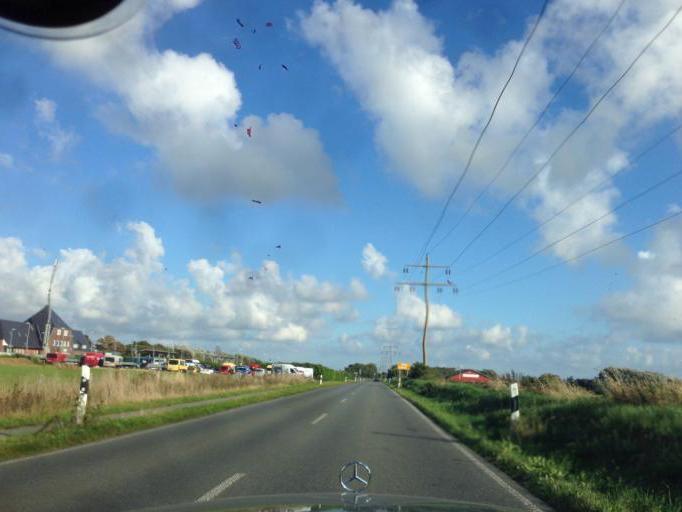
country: DE
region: Schleswig-Holstein
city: Keitum
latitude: 54.8892
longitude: 8.3661
